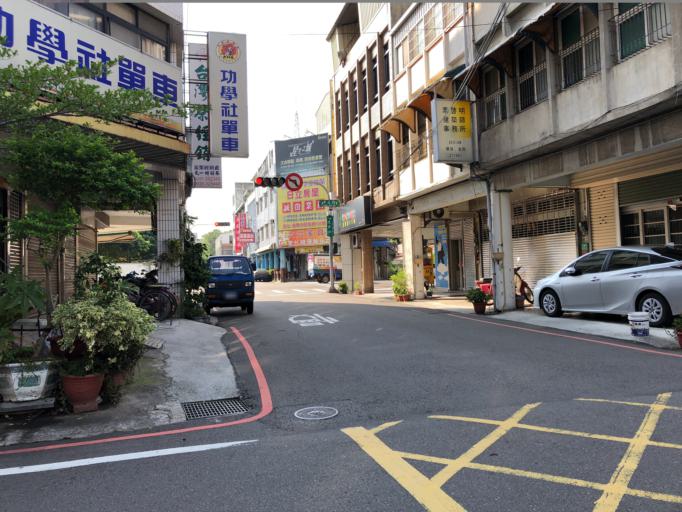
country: TW
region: Taiwan
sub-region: Miaoli
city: Miaoli
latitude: 24.5672
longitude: 120.8244
